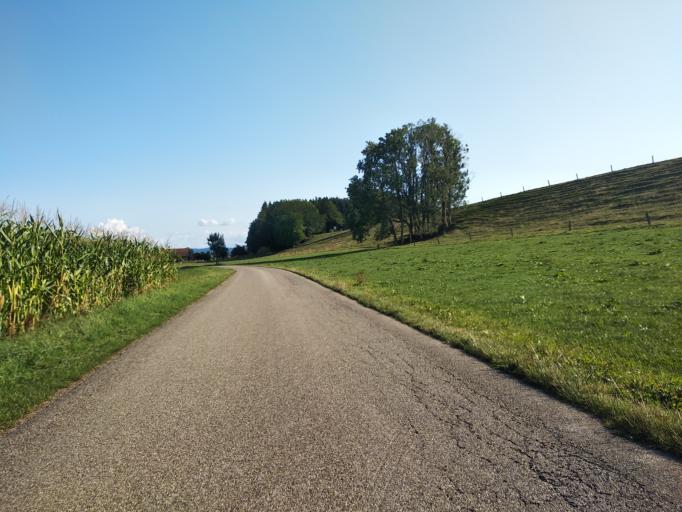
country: DE
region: Bavaria
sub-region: Swabia
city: Lautrach
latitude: 47.8822
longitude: 10.1159
